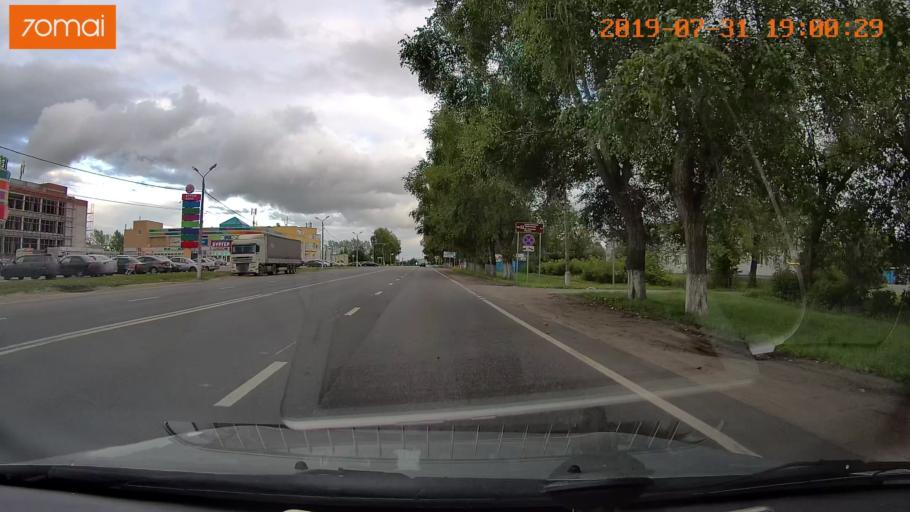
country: RU
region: Moskovskaya
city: Raduzhnyy
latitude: 55.1330
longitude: 38.7244
